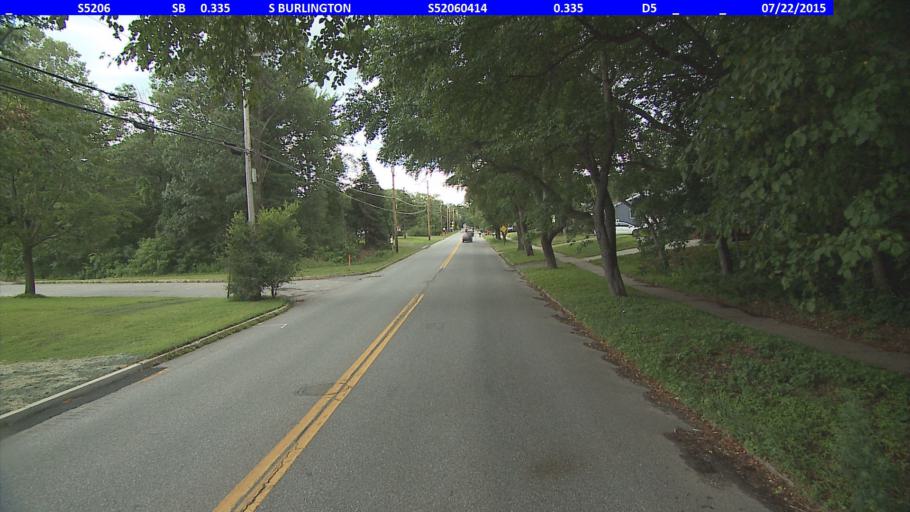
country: US
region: Vermont
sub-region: Chittenden County
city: South Burlington
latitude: 44.4753
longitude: -73.1653
